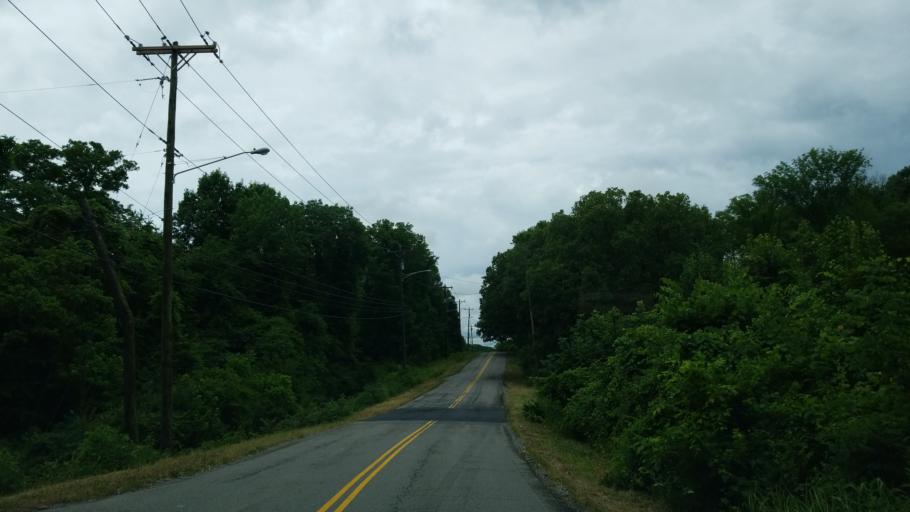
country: US
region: Tennessee
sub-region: Rutherford County
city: La Vergne
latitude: 36.1134
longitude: -86.6442
